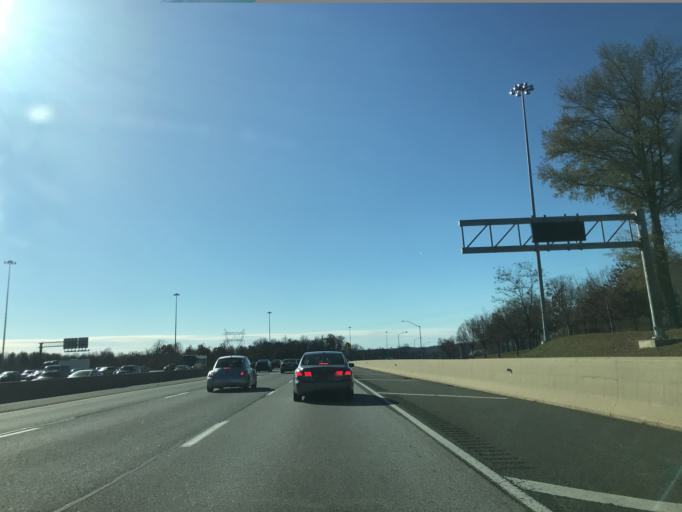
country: US
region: Maryland
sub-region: Cecil County
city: Perryville
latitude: 39.5893
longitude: -76.0726
